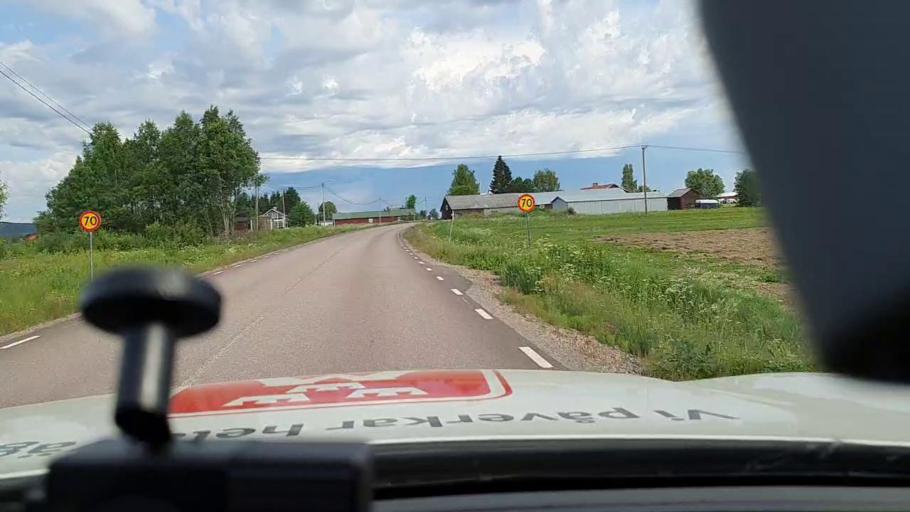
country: SE
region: Norrbotten
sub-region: Bodens Kommun
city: Saevast
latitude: 65.7017
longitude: 21.7703
